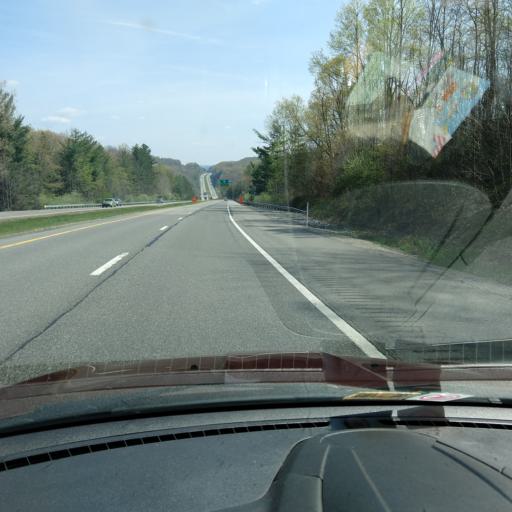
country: US
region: West Virginia
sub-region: Raleigh County
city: Bradley
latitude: 37.8882
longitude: -81.1870
